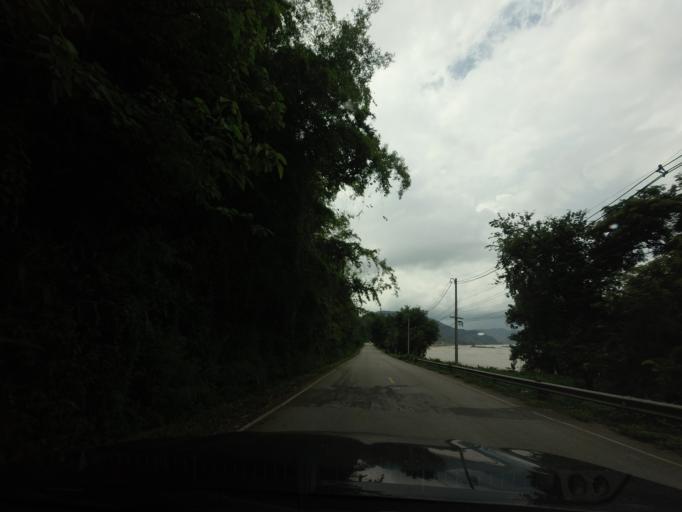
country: TH
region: Loei
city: Pak Chom
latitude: 18.0535
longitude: 101.8154
